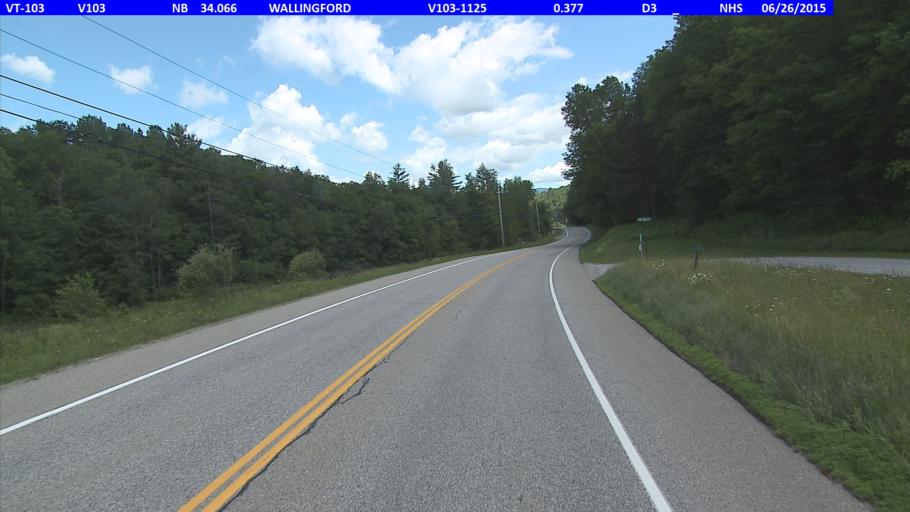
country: US
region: Vermont
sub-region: Rutland County
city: Rutland
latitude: 43.4557
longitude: -72.8762
